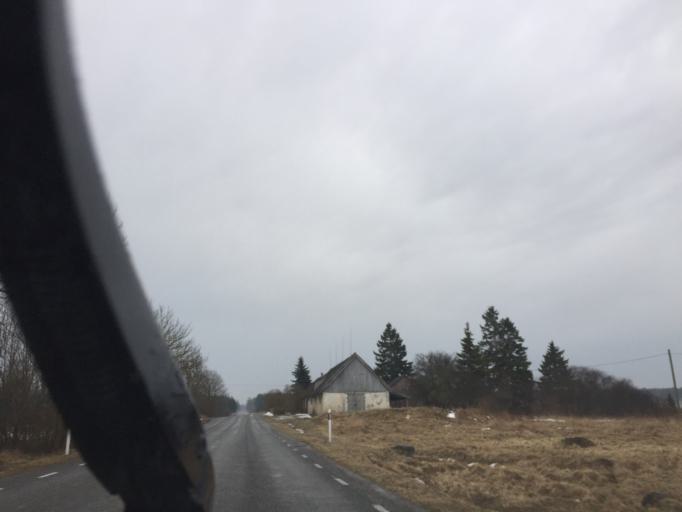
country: EE
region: Saare
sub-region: Orissaare vald
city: Orissaare
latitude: 58.5622
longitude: 23.0488
